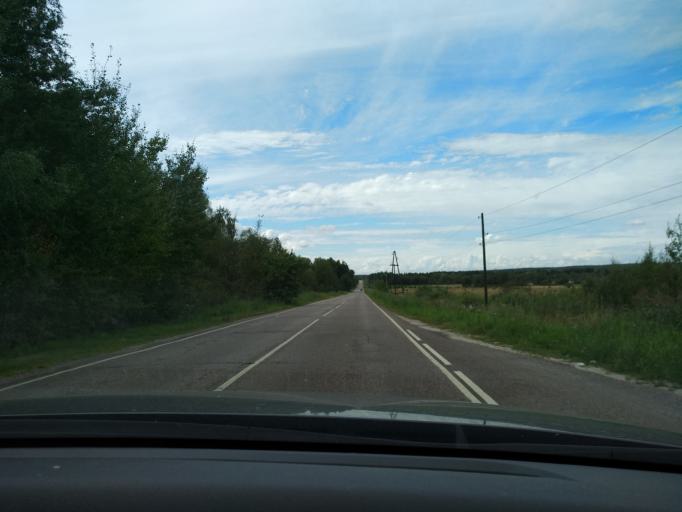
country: RU
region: Moskovskaya
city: Krasnyy Tkach
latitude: 55.3841
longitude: 39.1835
